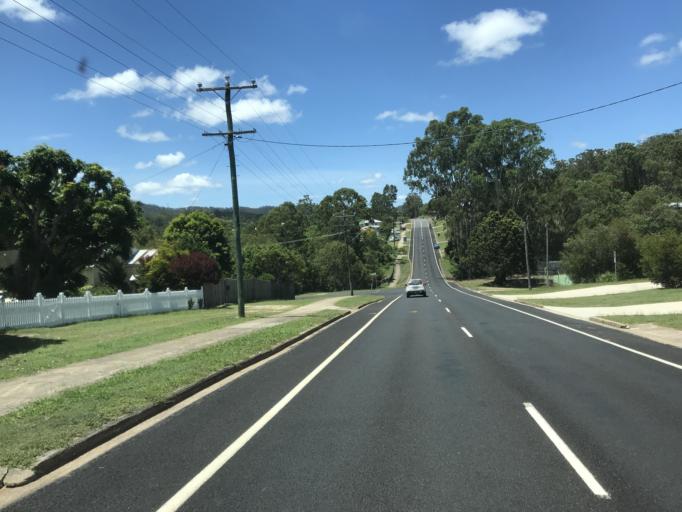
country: AU
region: Queensland
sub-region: Tablelands
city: Atherton
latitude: -17.3897
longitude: 145.3872
